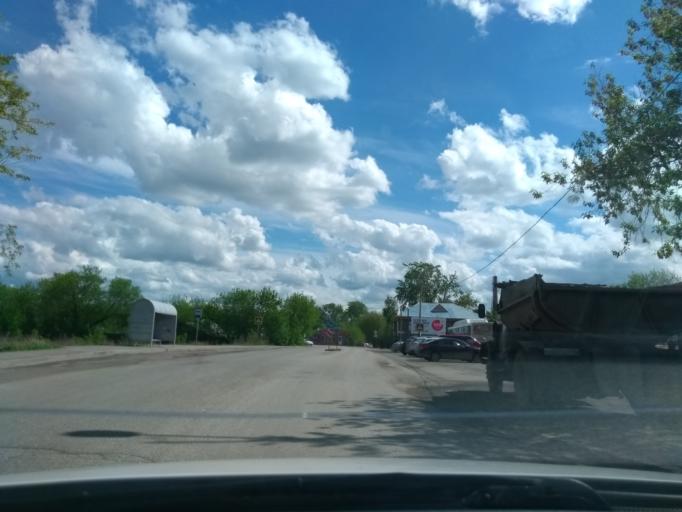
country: RU
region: Perm
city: Kondratovo
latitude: 58.0058
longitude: 56.1173
